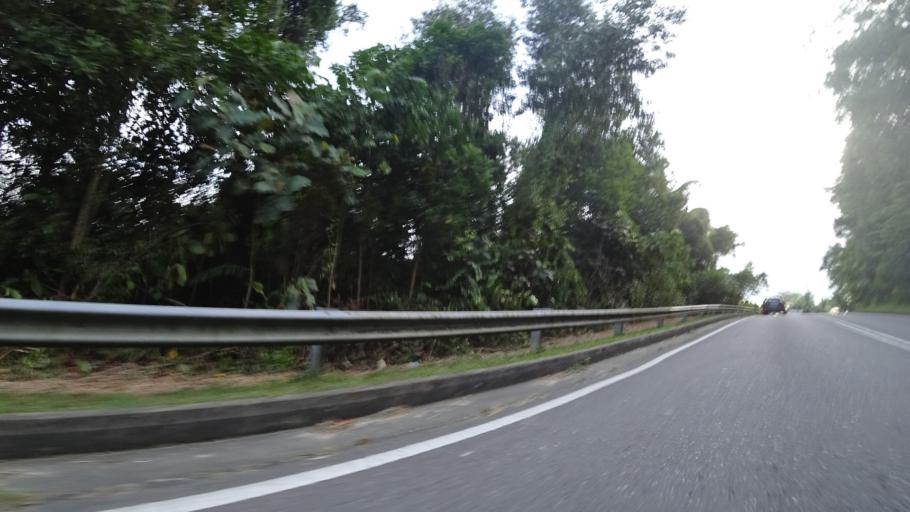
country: BN
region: Brunei and Muara
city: Bandar Seri Begawan
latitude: 4.8903
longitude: 114.9092
